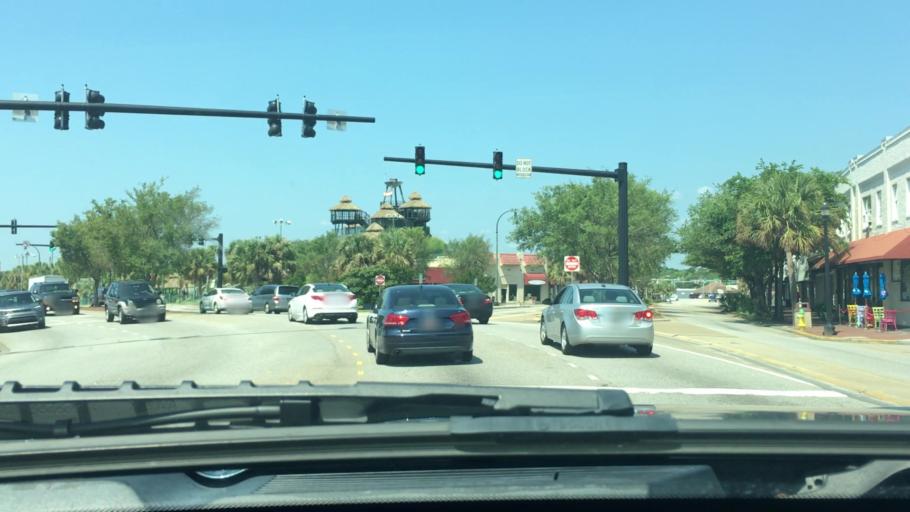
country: US
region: South Carolina
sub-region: Horry County
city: Myrtle Beach
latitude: 33.6934
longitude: -78.8831
